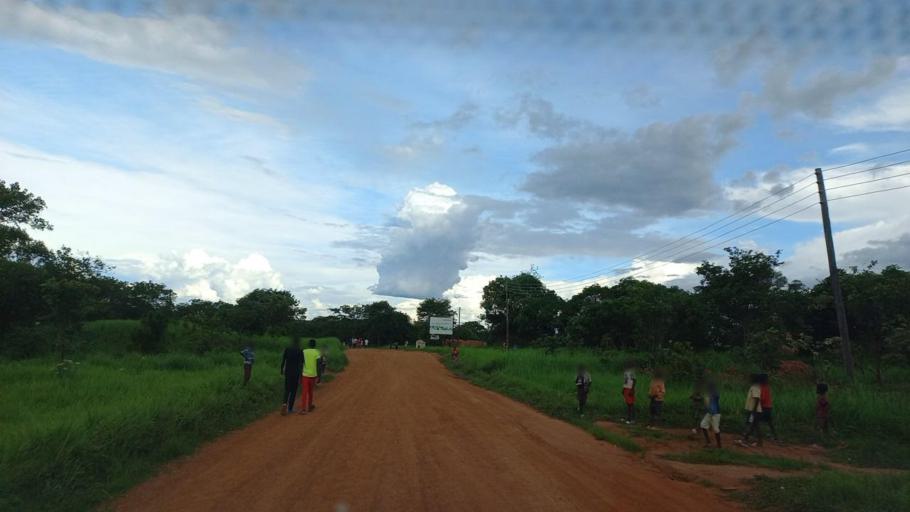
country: ZM
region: North-Western
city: Mwinilunga
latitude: -11.7587
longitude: 24.4274
